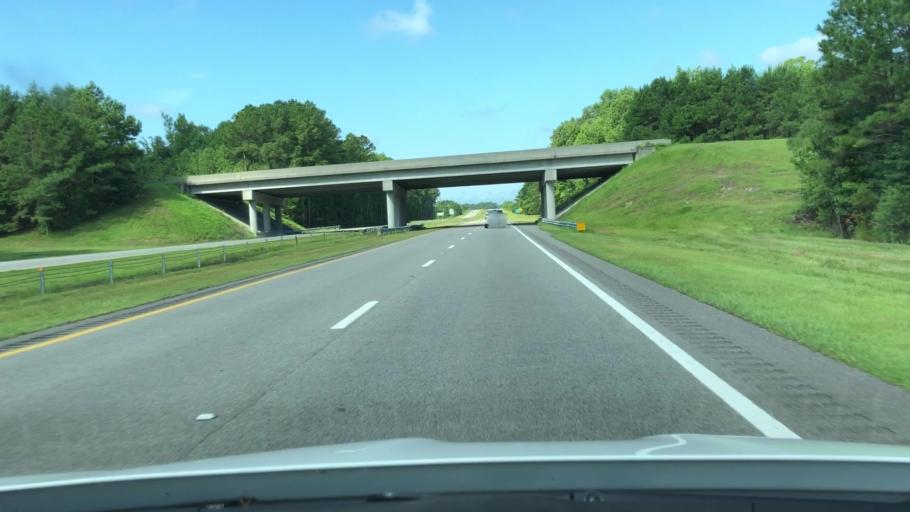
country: US
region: North Carolina
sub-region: Chowan County
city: Edenton
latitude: 36.0921
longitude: -76.5714
